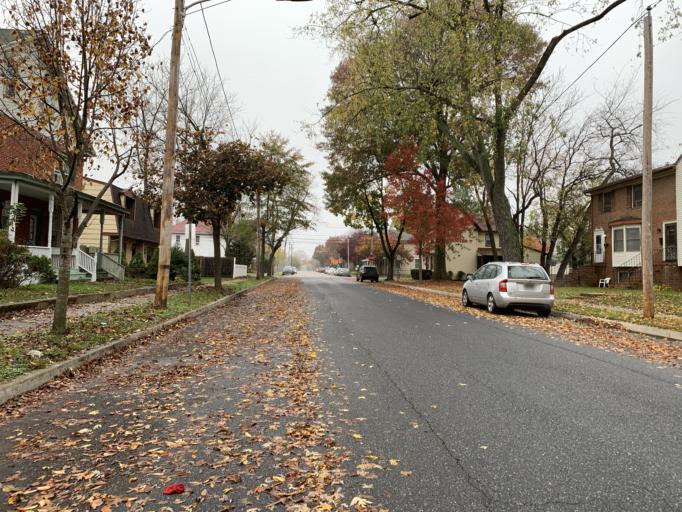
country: US
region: Delaware
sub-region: Kent County
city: Dover
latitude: 39.1641
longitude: -75.5307
